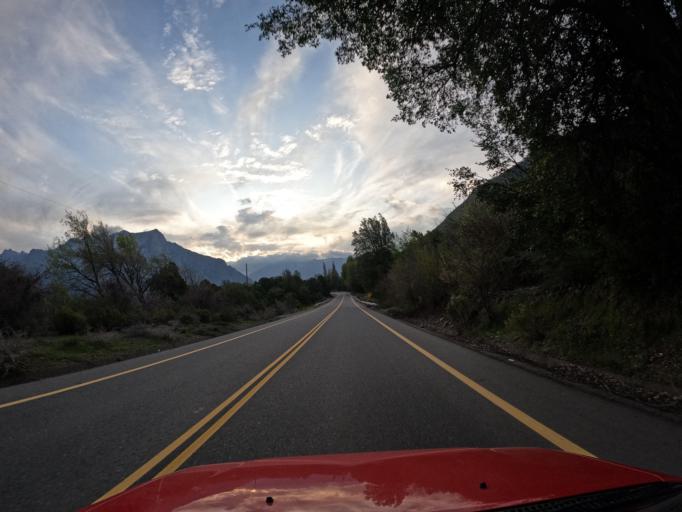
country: CL
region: Maule
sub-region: Provincia de Linares
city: Colbun
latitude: -35.7143
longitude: -71.0422
